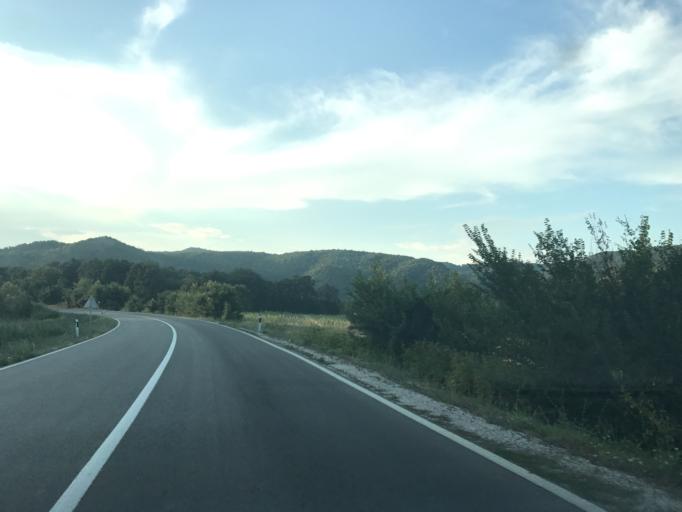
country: RS
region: Central Serbia
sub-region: Zajecarski Okrug
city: Zajecar
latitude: 43.9164
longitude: 22.1987
